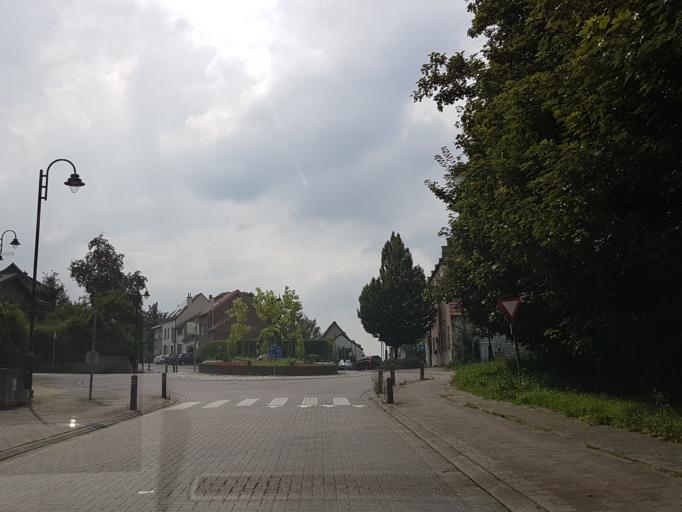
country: BE
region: Flanders
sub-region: Provincie Vlaams-Brabant
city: Kortenberg
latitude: 50.8733
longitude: 4.5256
